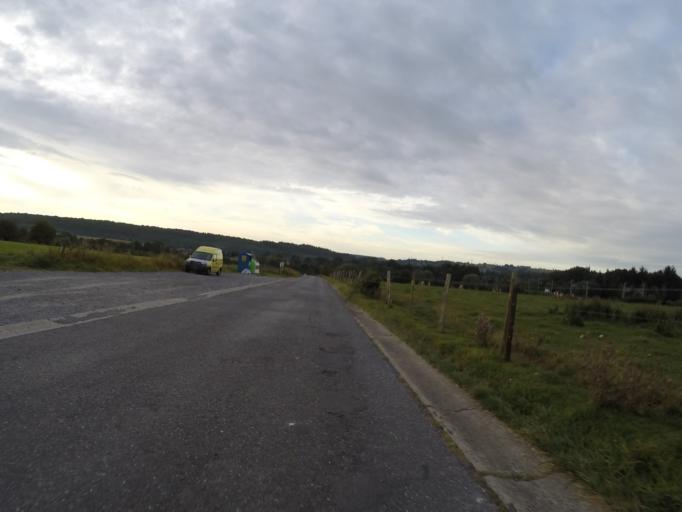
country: BE
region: Wallonia
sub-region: Province de Namur
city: Ciney
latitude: 50.3317
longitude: 5.0651
